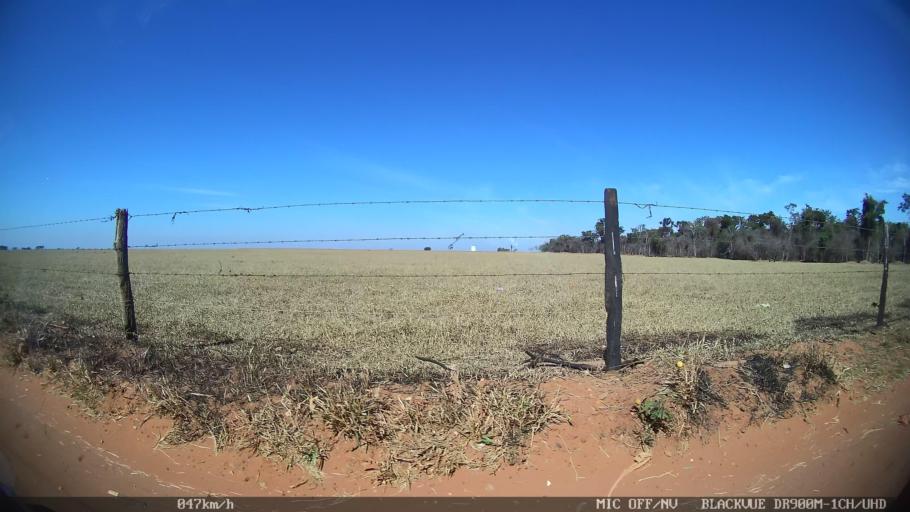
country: BR
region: Sao Paulo
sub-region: Sao Jose Do Rio Preto
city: Sao Jose do Rio Preto
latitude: -20.7419
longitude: -49.4265
